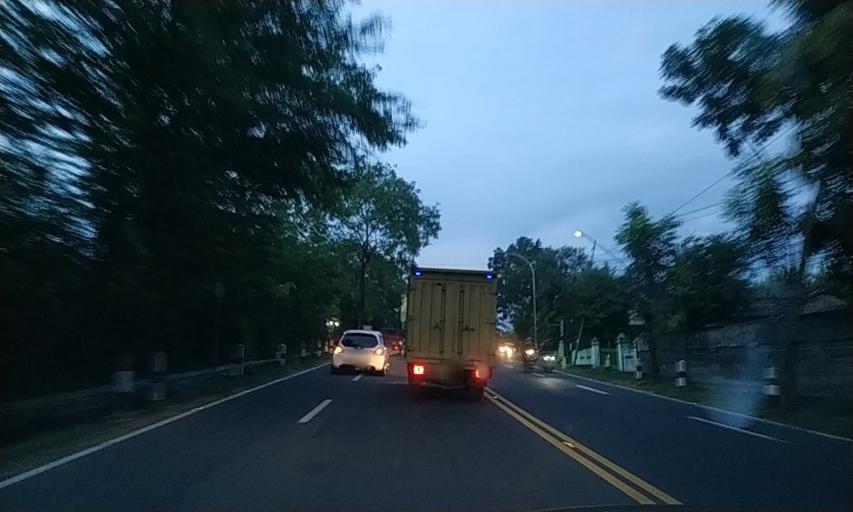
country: ID
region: Daerah Istimewa Yogyakarta
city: Godean
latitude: -7.8288
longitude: 110.2217
